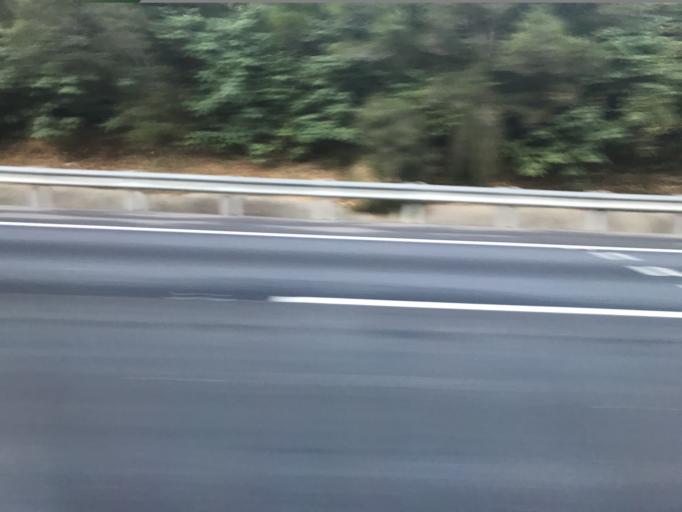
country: TW
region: Taiwan
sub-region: Miaoli
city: Miaoli
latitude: 24.6254
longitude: 120.8136
